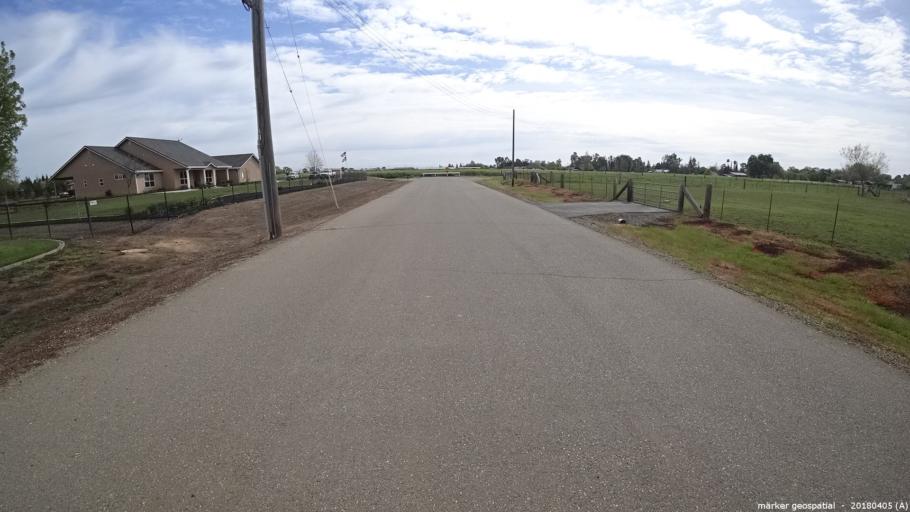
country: US
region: California
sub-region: Sacramento County
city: Galt
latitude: 38.2709
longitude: -121.3343
